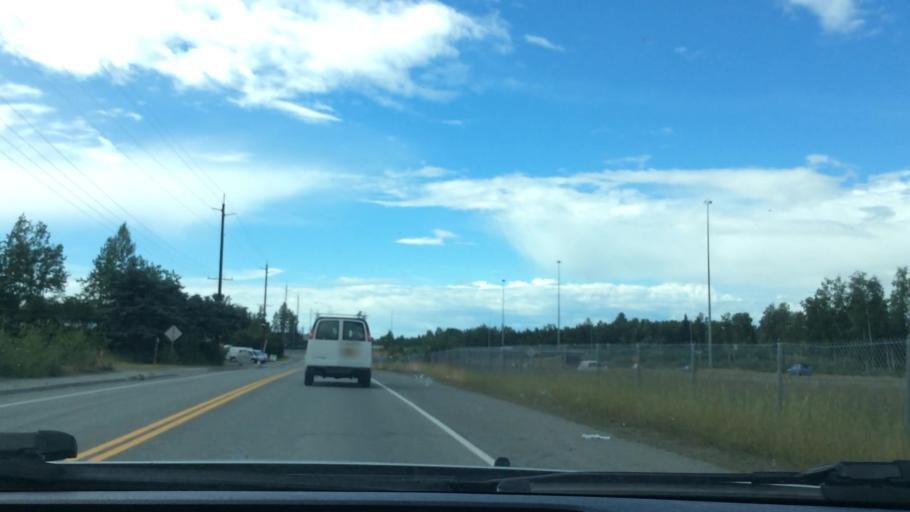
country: US
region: Alaska
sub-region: Anchorage Municipality
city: Anchorage
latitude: 61.2242
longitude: -149.7717
